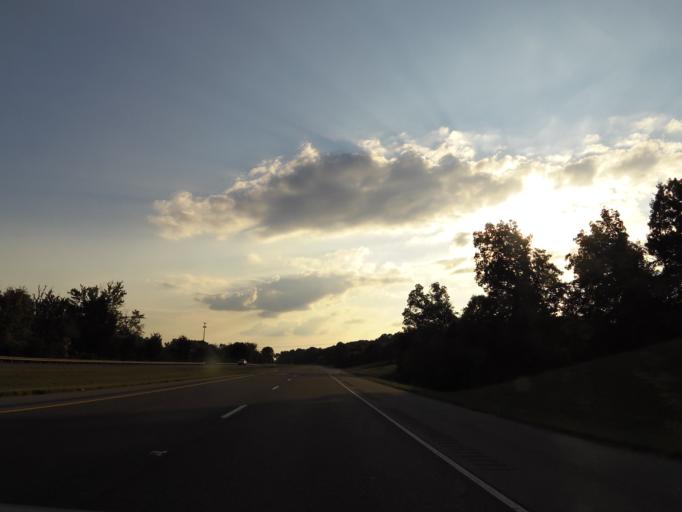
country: US
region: Tennessee
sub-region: Knox County
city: Mascot
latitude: 36.0457
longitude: -83.8190
